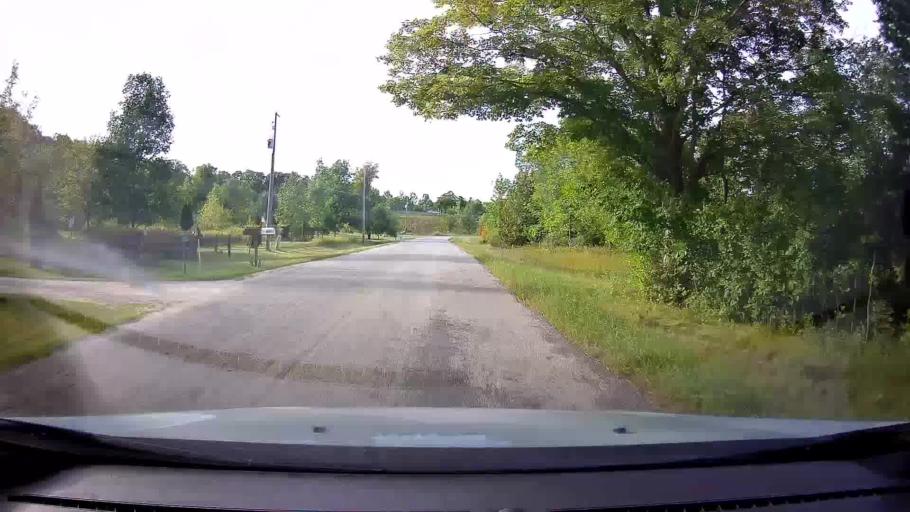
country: US
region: Wisconsin
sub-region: Door County
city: Sturgeon Bay
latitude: 45.1797
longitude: -87.1454
